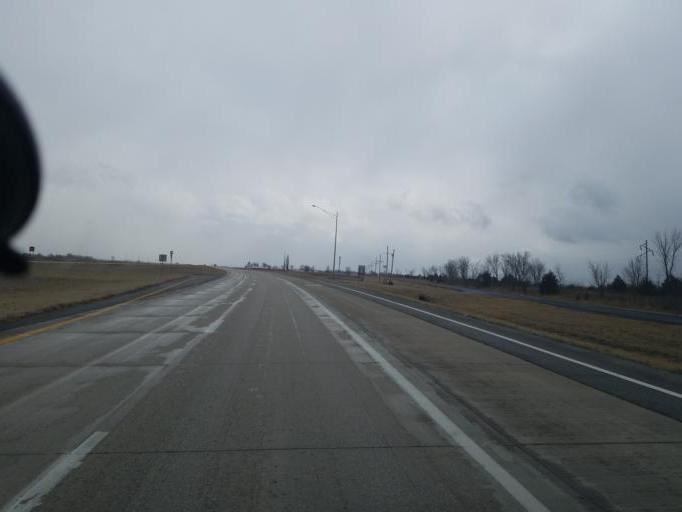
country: US
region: Missouri
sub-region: Randolph County
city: Moberly
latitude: 39.5331
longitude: -92.4461
